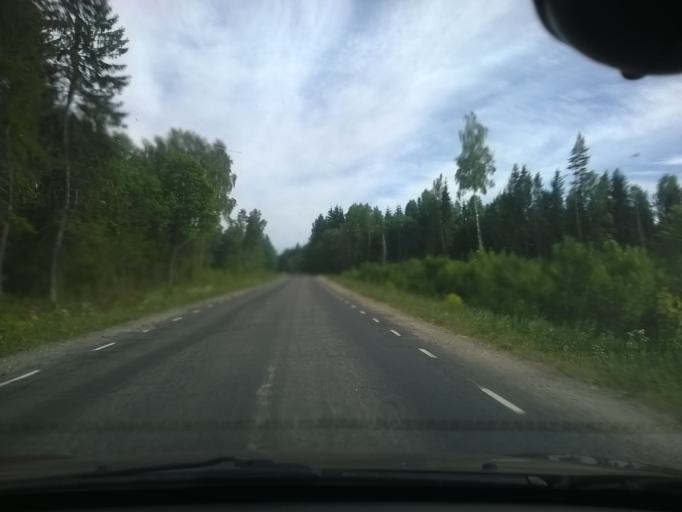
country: EE
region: Harju
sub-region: Raasiku vald
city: Raasiku
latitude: 59.2914
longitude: 25.1833
